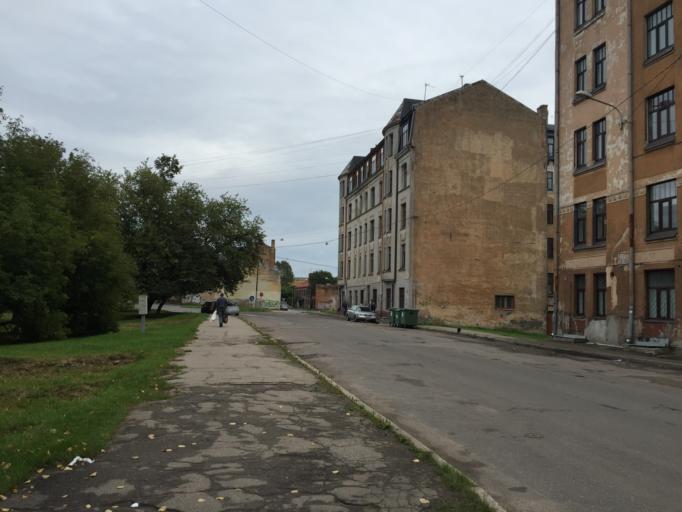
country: LV
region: Riga
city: Riga
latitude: 56.9396
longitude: 24.1326
